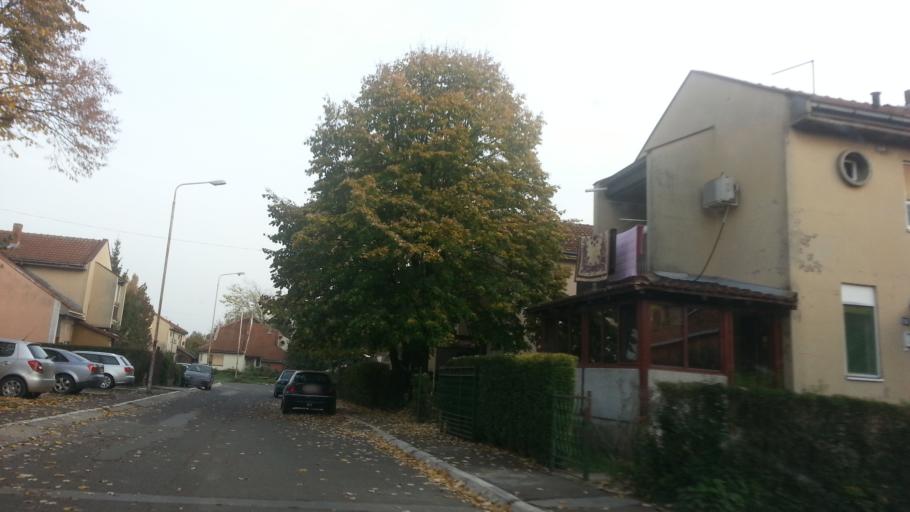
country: RS
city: Novi Banovci
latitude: 44.8951
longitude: 20.2845
